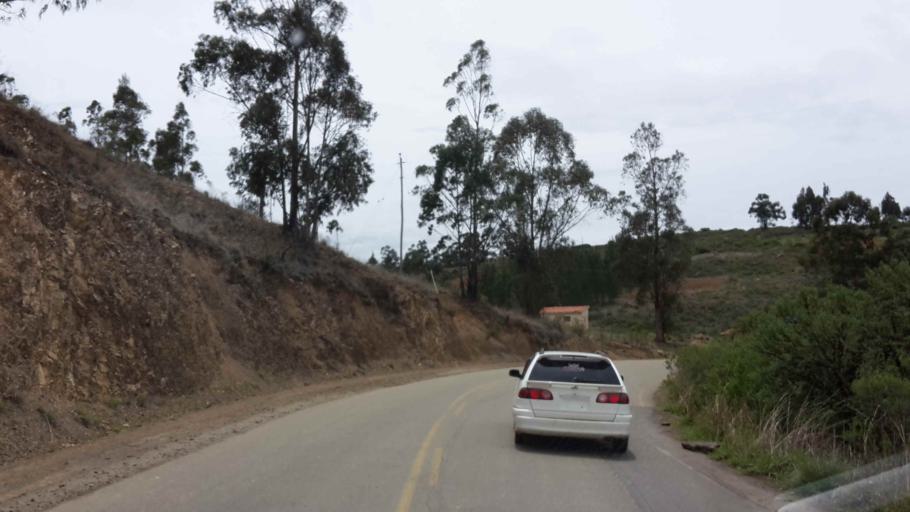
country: BO
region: Cochabamba
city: Totora
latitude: -17.7209
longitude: -65.2019
